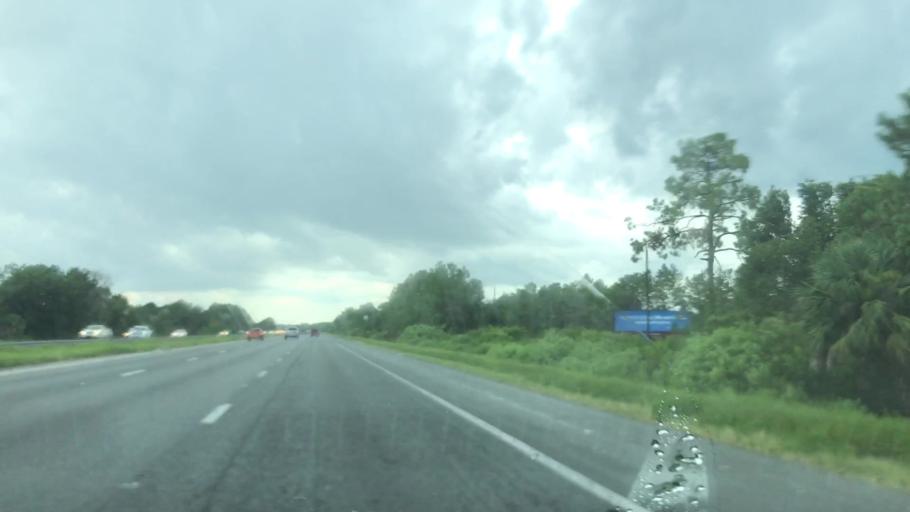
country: US
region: Florida
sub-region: Volusia County
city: Ormond-by-the-Sea
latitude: 29.3139
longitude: -81.1319
